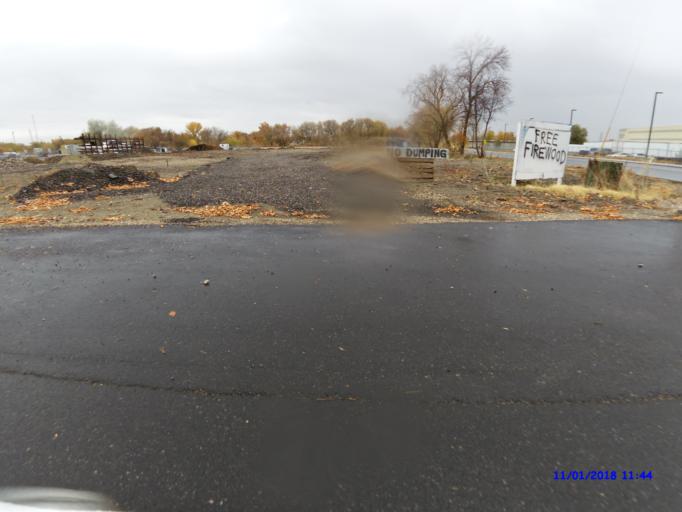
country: US
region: Utah
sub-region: Weber County
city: Ogden
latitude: 41.2366
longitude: -111.9872
